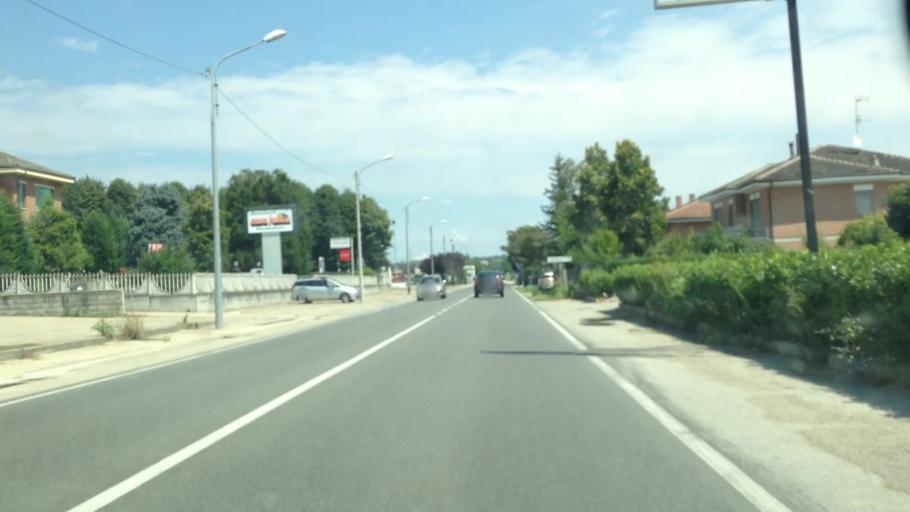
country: IT
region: Piedmont
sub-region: Provincia di Asti
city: Castell'Alfero
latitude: 44.9631
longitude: 8.2255
